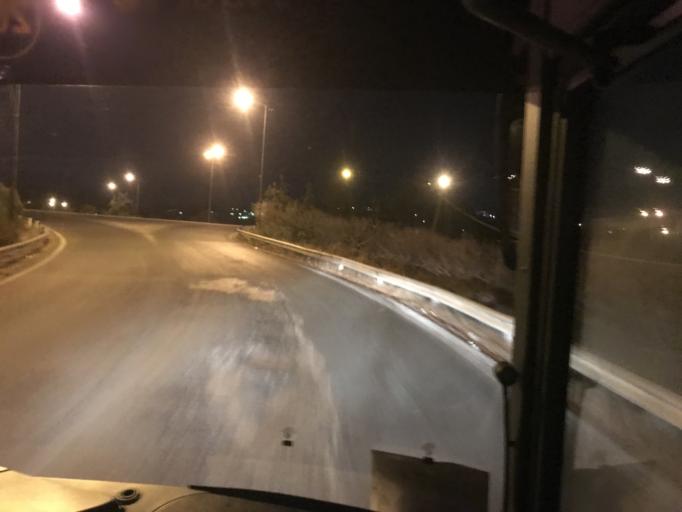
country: GR
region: Crete
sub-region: Nomos Irakleiou
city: Nea Alikarnassos
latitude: 35.3331
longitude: 25.1575
